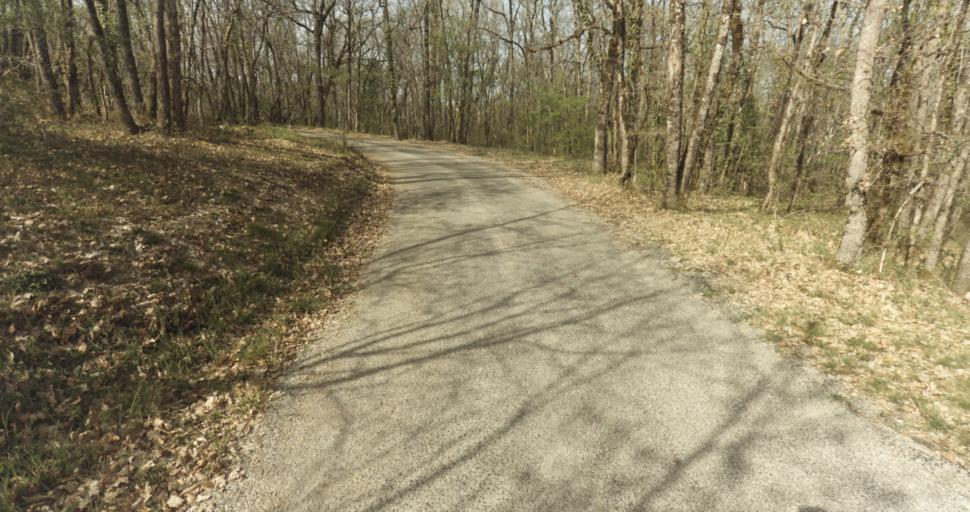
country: FR
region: Midi-Pyrenees
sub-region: Departement du Tarn-et-Garonne
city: Lafrancaise
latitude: 44.1533
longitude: 1.1763
